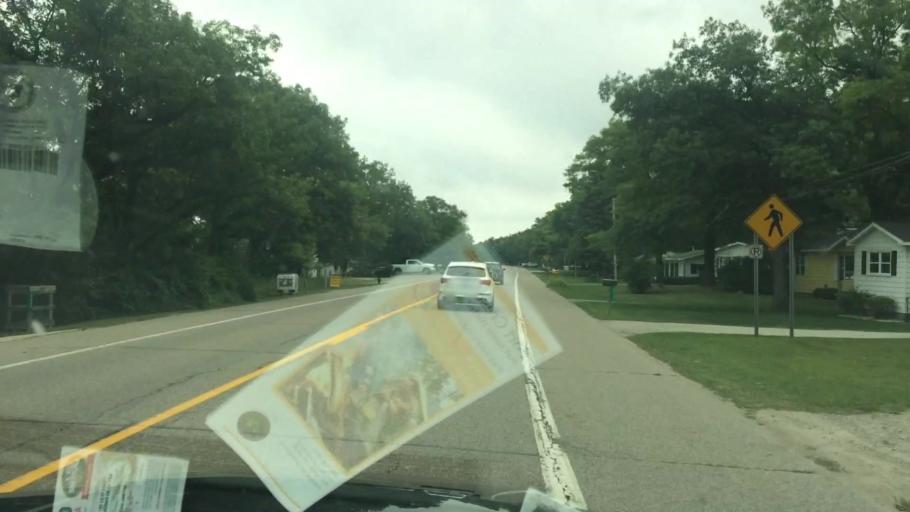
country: US
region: Michigan
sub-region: Huron County
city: Pigeon
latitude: 43.9819
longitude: -83.1949
